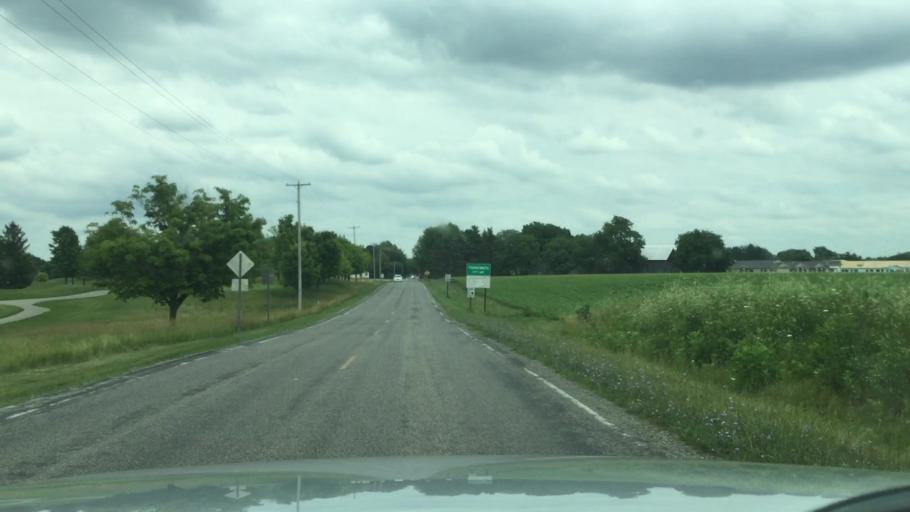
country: US
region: Michigan
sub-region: Saginaw County
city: Frankenmuth
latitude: 43.3218
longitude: -83.7496
